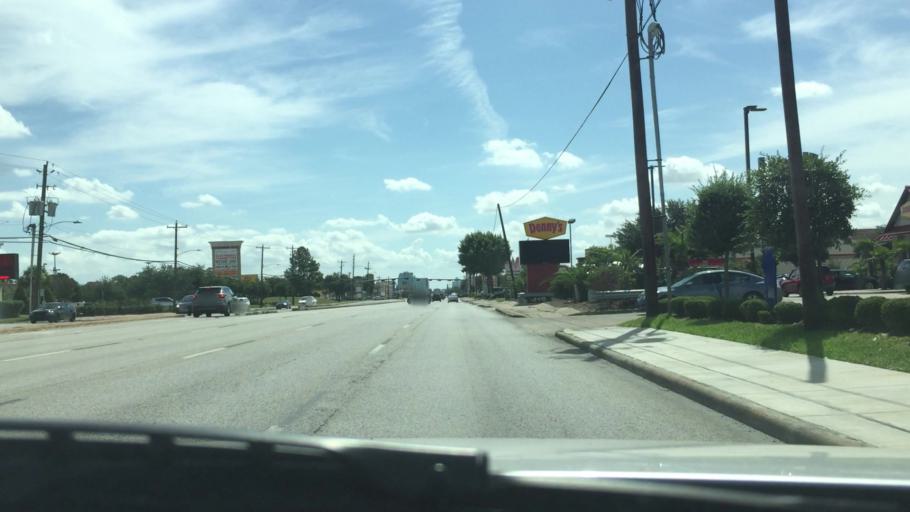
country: US
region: Texas
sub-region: Fort Bend County
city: Mission Bend
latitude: 29.7361
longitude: -95.6014
